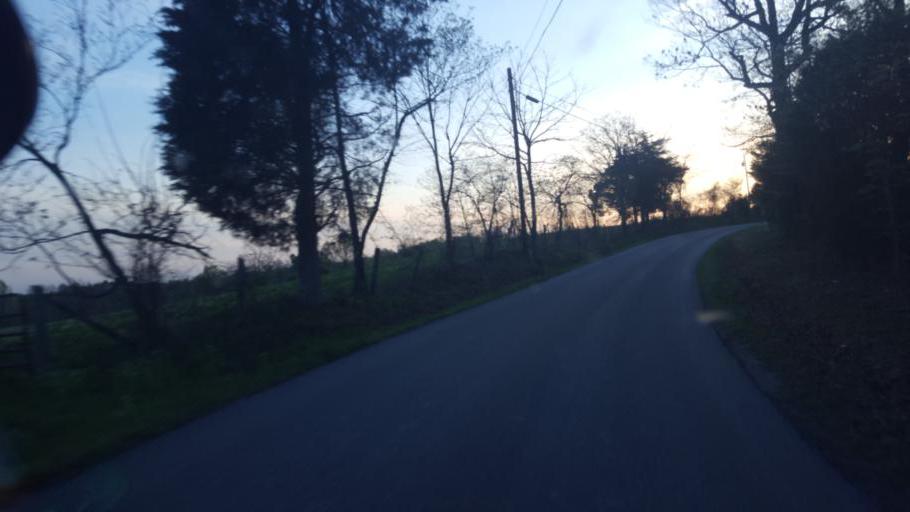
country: US
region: Kentucky
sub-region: Hart County
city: Munfordville
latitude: 37.2696
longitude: -85.9454
